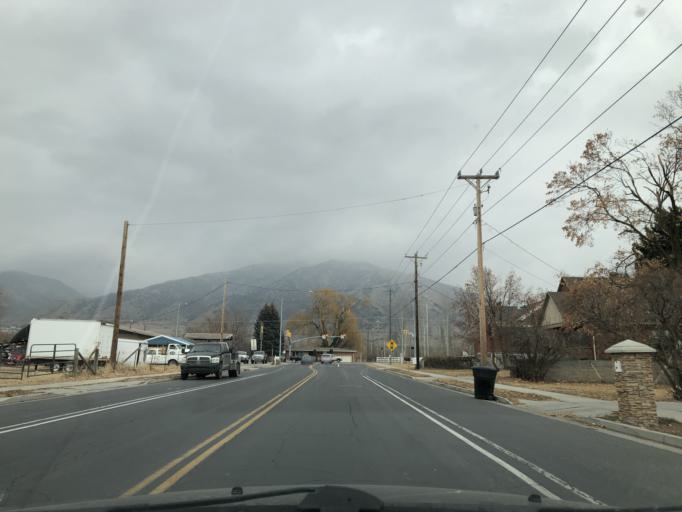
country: US
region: Utah
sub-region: Cache County
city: Nibley
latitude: 41.6747
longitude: -111.8350
